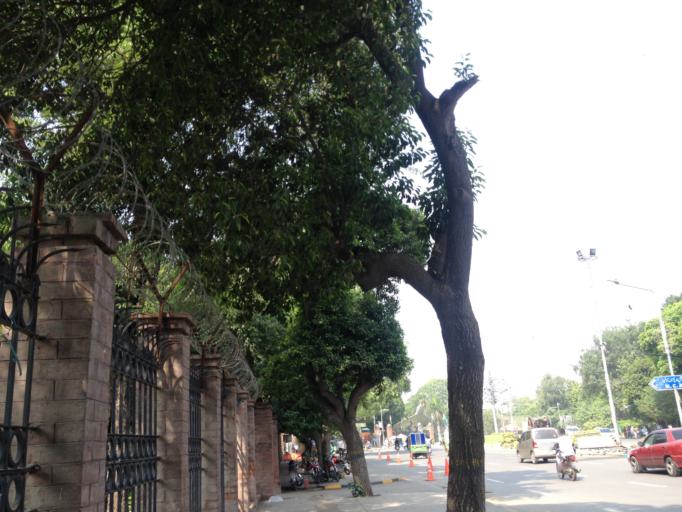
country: PK
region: Punjab
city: Lahore
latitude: 31.5687
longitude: 74.3081
